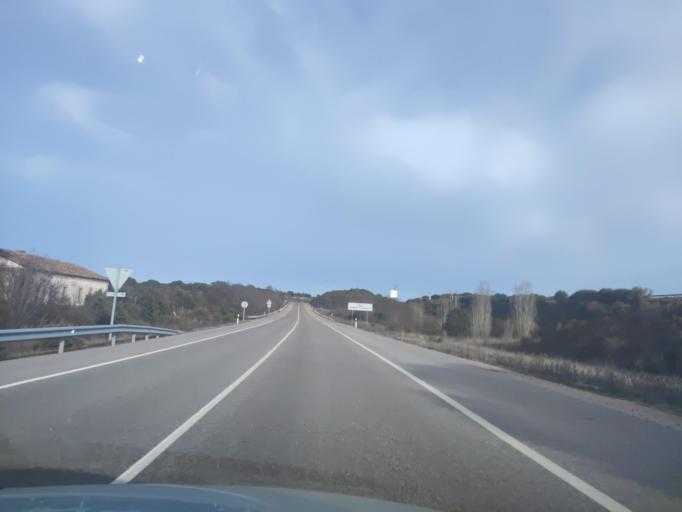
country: ES
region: Castille and Leon
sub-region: Provincia de Salamanca
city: Espeja
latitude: 40.5917
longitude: -6.7036
